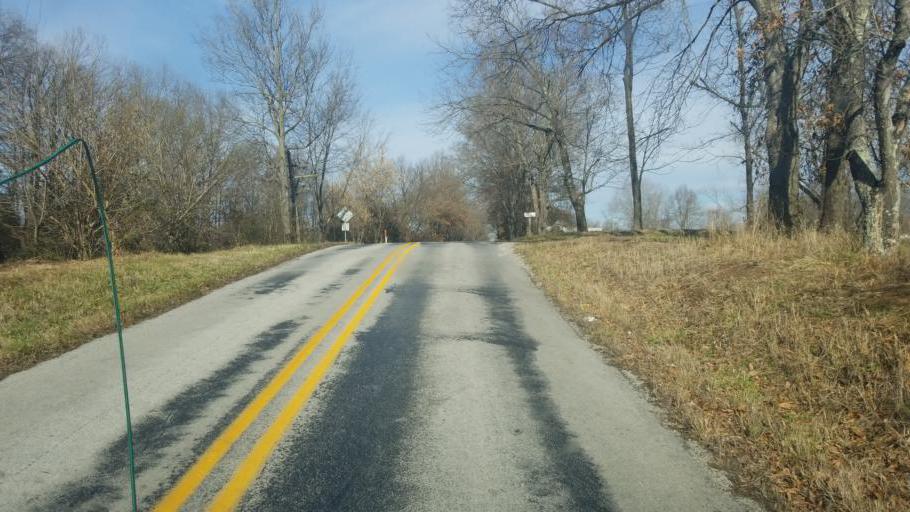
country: US
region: Illinois
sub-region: Jackson County
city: Carbondale
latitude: 37.6869
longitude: -89.2108
